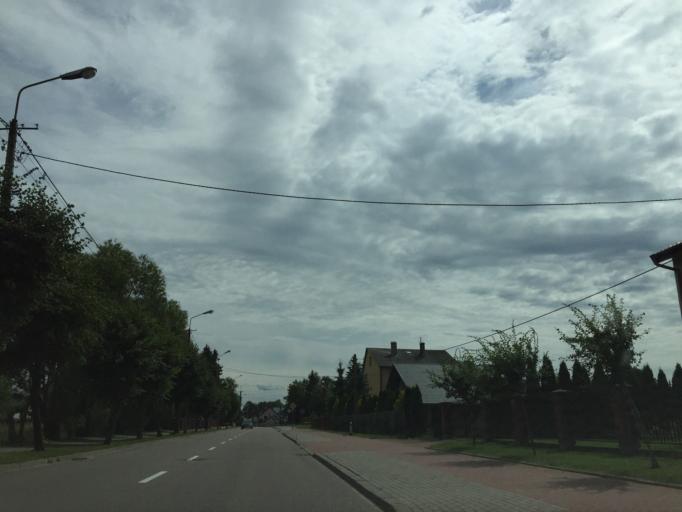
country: PL
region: Podlasie
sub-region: Powiat bielski
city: Bielsk Podlaski
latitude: 52.7457
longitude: 23.1905
